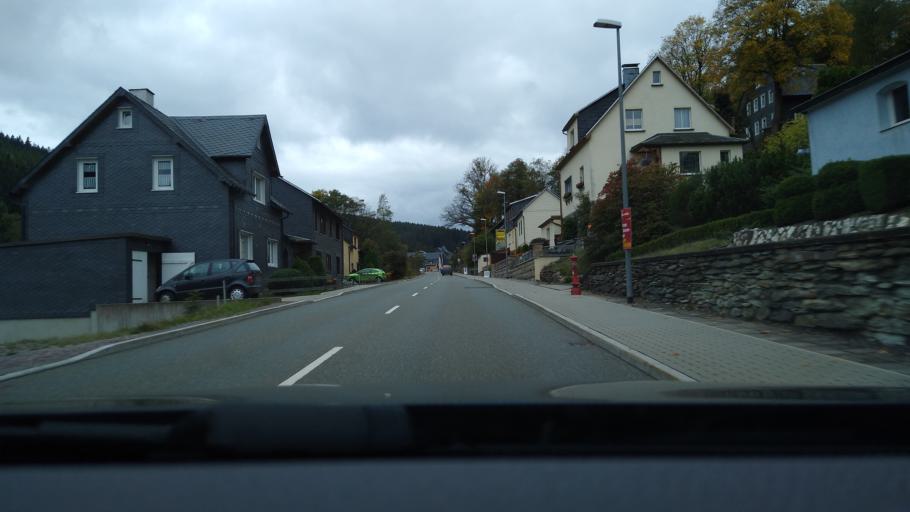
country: DE
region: Thuringia
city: Lichte
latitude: 50.5234
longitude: 11.1889
